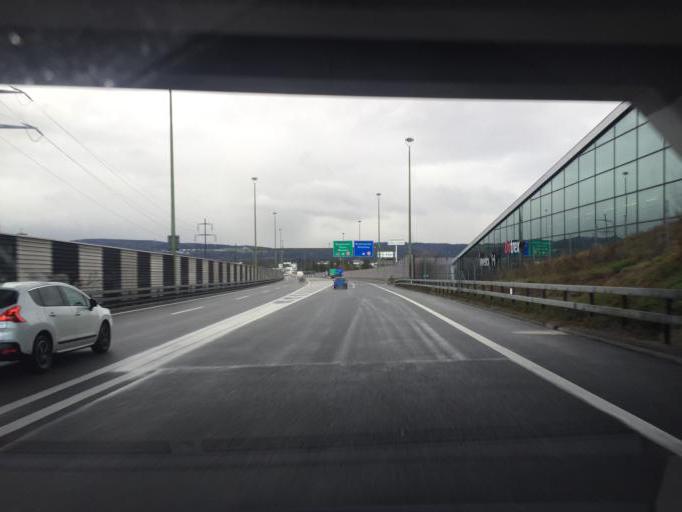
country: CH
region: Zurich
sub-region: Bezirk Uster
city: Bruttisellen
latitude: 47.4199
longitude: 8.6323
